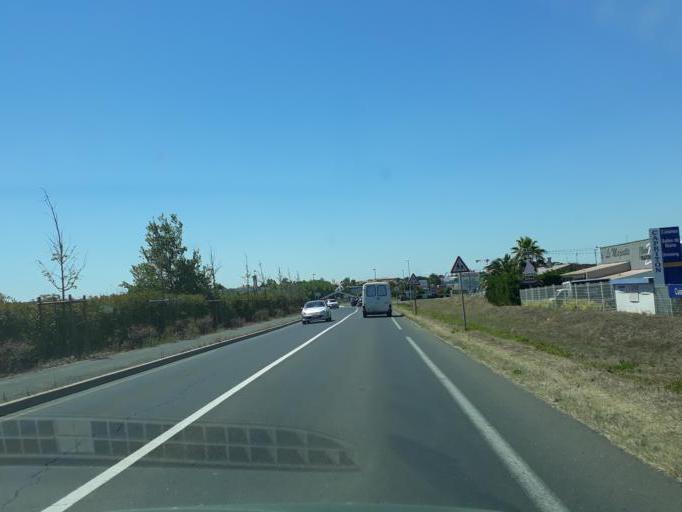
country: FR
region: Languedoc-Roussillon
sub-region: Departement de l'Herault
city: Agde
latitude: 43.3077
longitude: 3.4975
